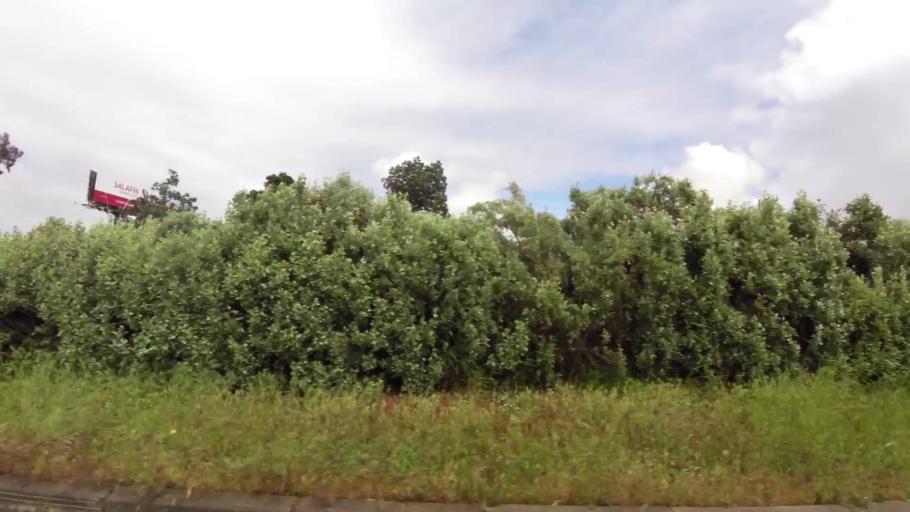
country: MA
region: Grand Casablanca
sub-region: Casablanca
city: Casablanca
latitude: 33.5321
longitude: -7.6384
